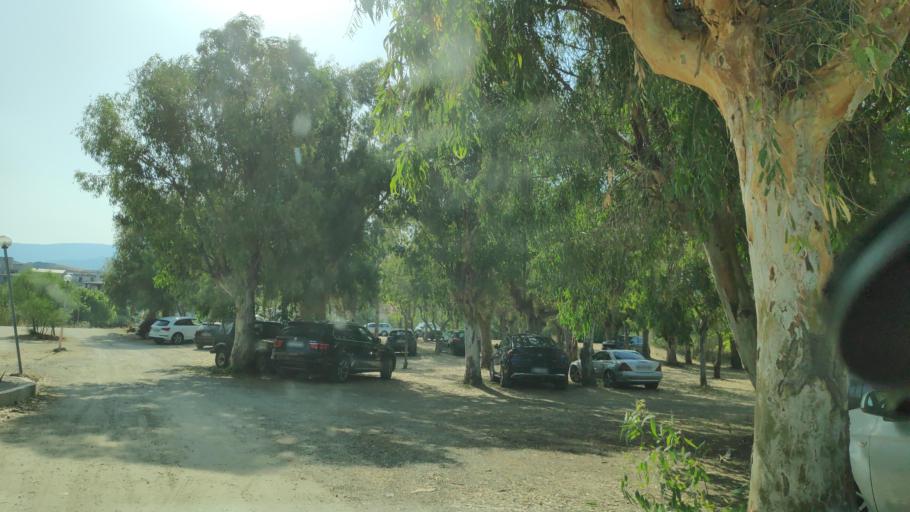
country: IT
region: Calabria
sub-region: Provincia di Catanzaro
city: Badolato Marina
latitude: 38.5781
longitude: 16.5688
